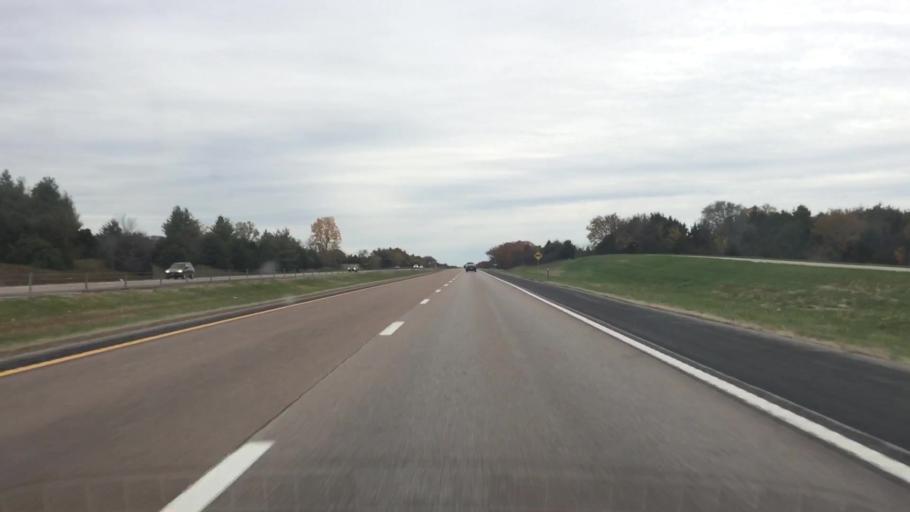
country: US
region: Missouri
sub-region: Boone County
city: Ashland
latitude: 38.7127
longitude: -92.2544
